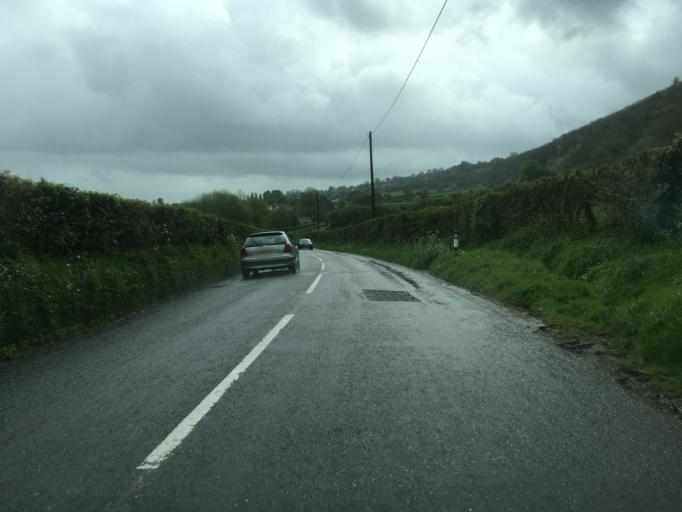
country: GB
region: England
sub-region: Bath and North East Somerset
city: Compton Martin
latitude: 51.3147
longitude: -2.6698
